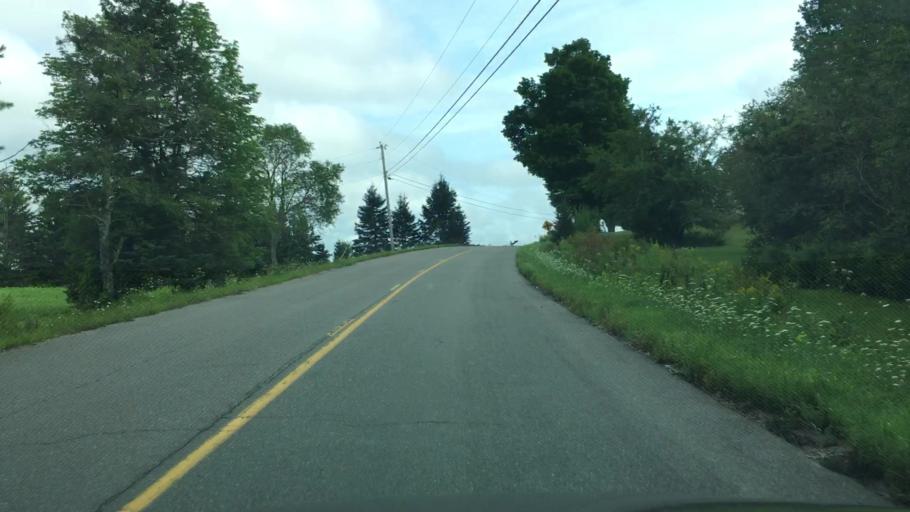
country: US
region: Maine
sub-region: Waldo County
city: Winterport
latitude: 44.6817
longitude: -68.8686
